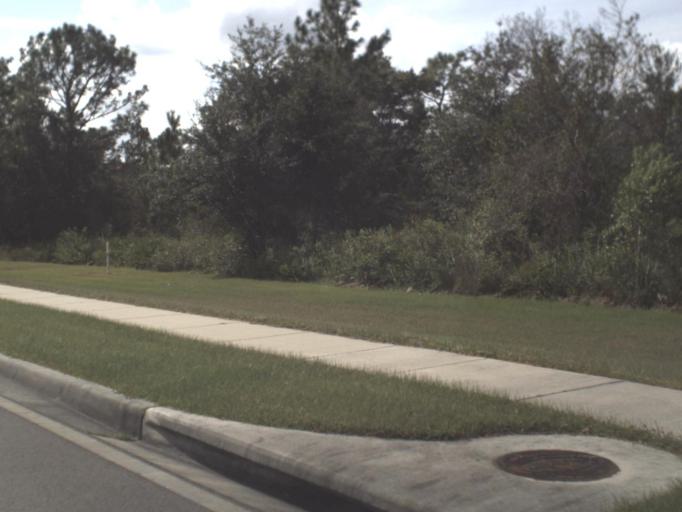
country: US
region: Florida
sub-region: Osceola County
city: Campbell
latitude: 28.2475
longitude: -81.4876
